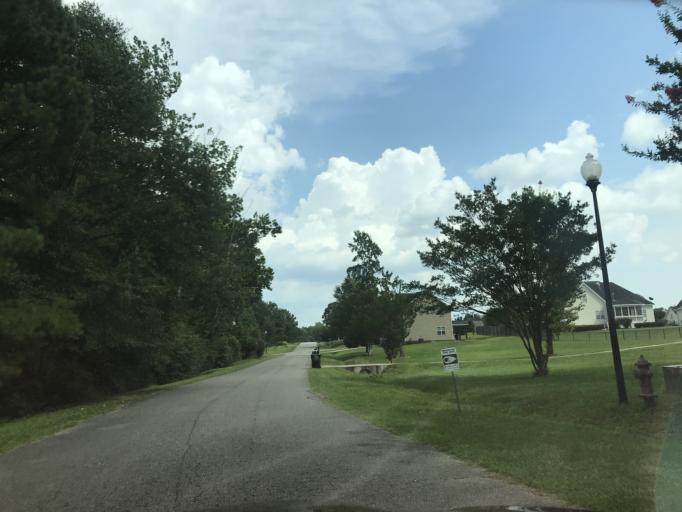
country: US
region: North Carolina
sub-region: Johnston County
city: Four Oaks
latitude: 35.5135
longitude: -78.5037
